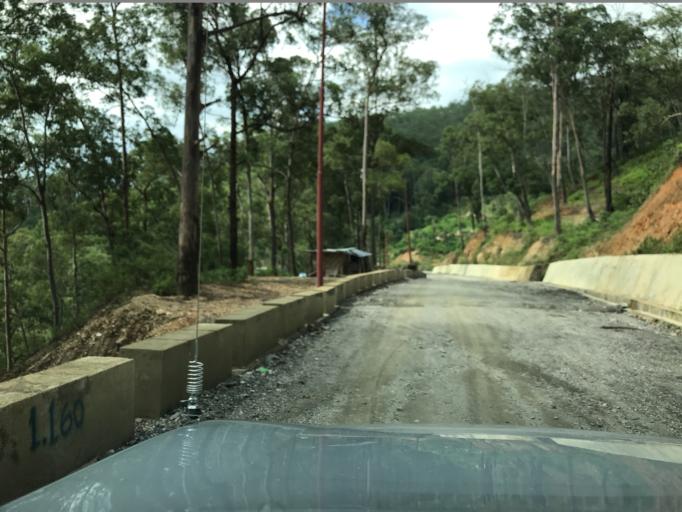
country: TL
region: Aileu
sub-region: Aileu Villa
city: Aileu
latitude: -8.6625
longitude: 125.5315
